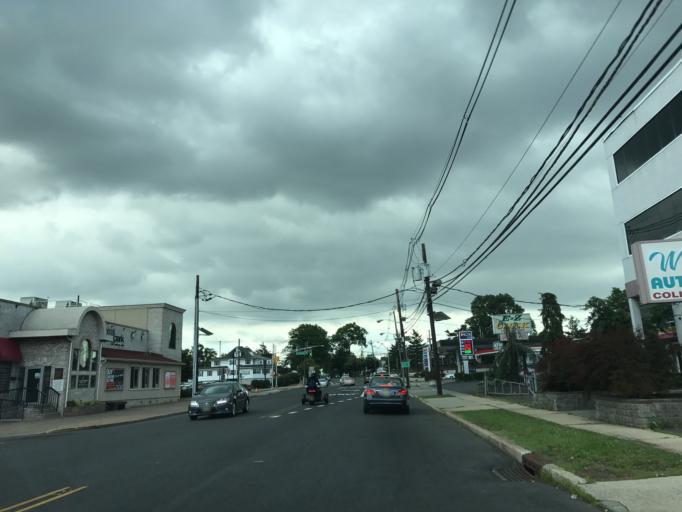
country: US
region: New Jersey
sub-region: Union County
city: Winfield
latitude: 40.6379
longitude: -74.2653
